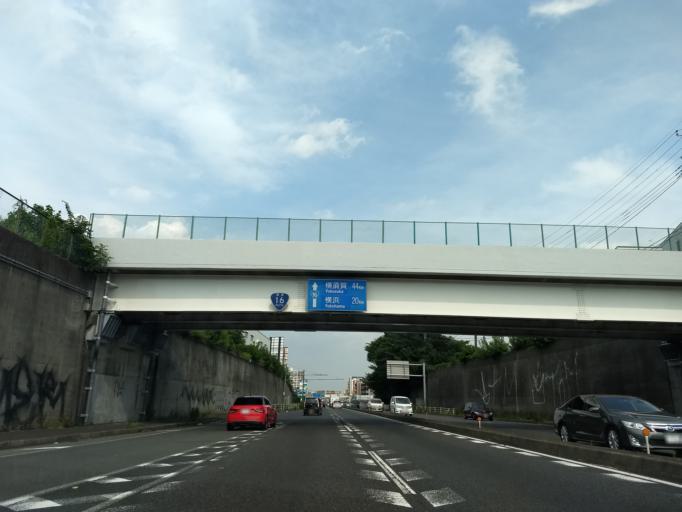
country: JP
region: Tokyo
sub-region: Machida-shi
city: Machida
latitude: 35.5142
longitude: 139.4601
